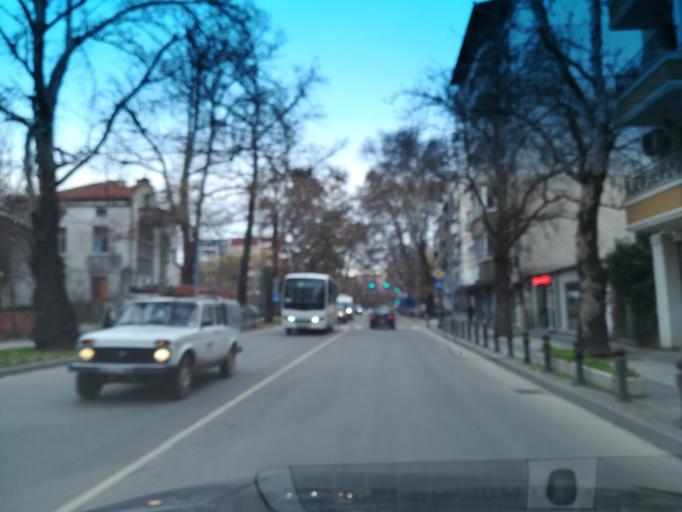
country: BG
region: Plovdiv
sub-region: Obshtina Plovdiv
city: Plovdiv
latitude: 42.1446
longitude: 24.7319
